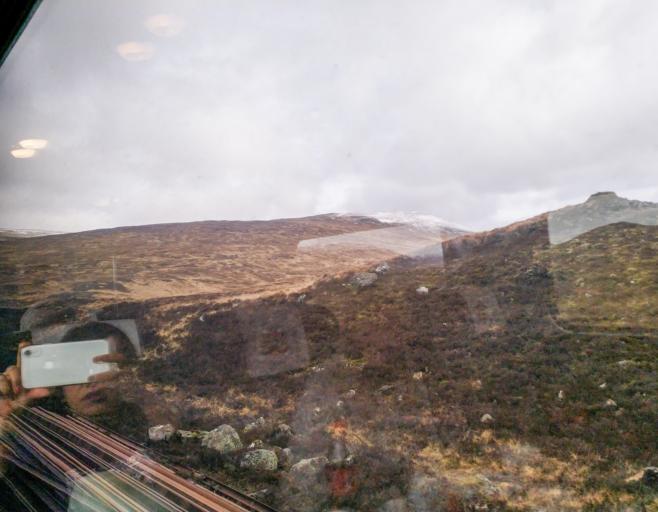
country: GB
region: Scotland
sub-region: Highland
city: Spean Bridge
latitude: 56.7659
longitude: -4.6984
